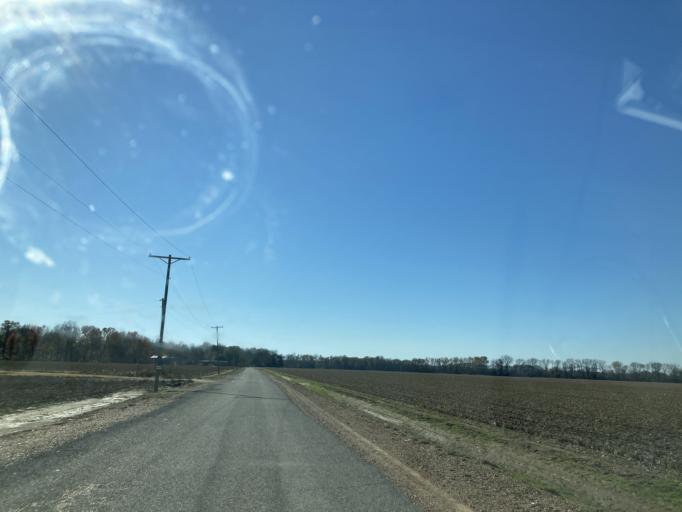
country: US
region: Mississippi
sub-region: Sharkey County
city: Rolling Fork
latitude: 32.8201
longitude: -90.7297
